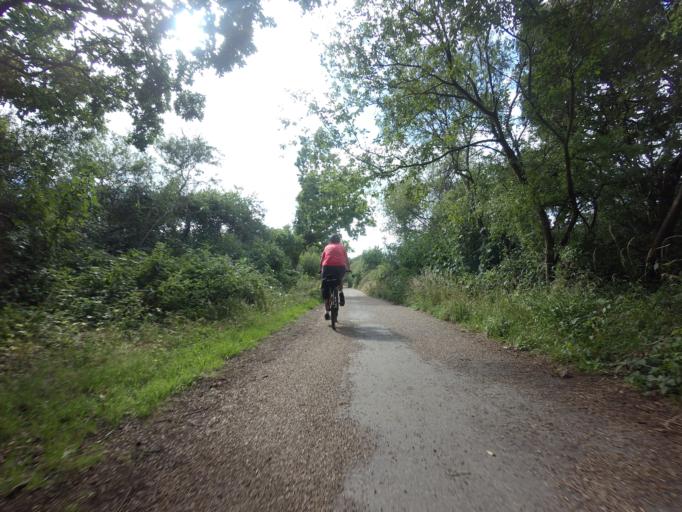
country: GB
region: England
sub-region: East Sussex
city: Hailsham
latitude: 50.8196
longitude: 0.2635
